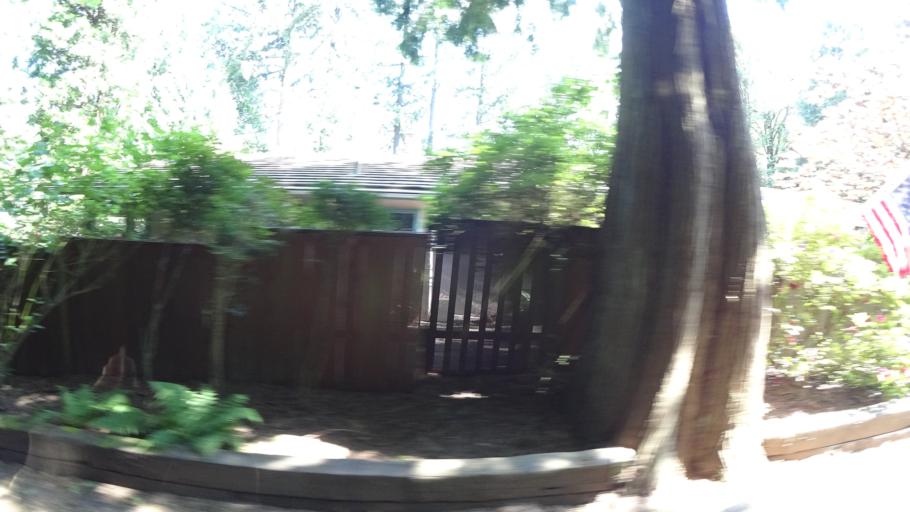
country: US
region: Oregon
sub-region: Washington County
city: West Haven-Sylvan
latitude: 45.5193
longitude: -122.7271
